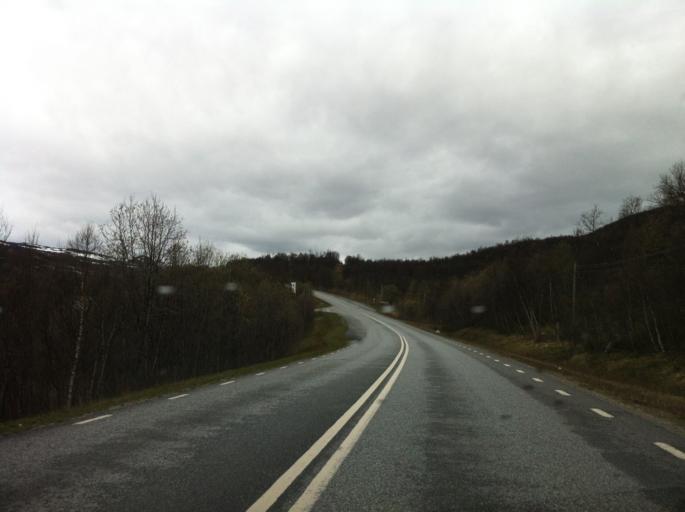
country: NO
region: Sor-Trondelag
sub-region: Tydal
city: Aas
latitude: 62.5680
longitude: 12.2463
